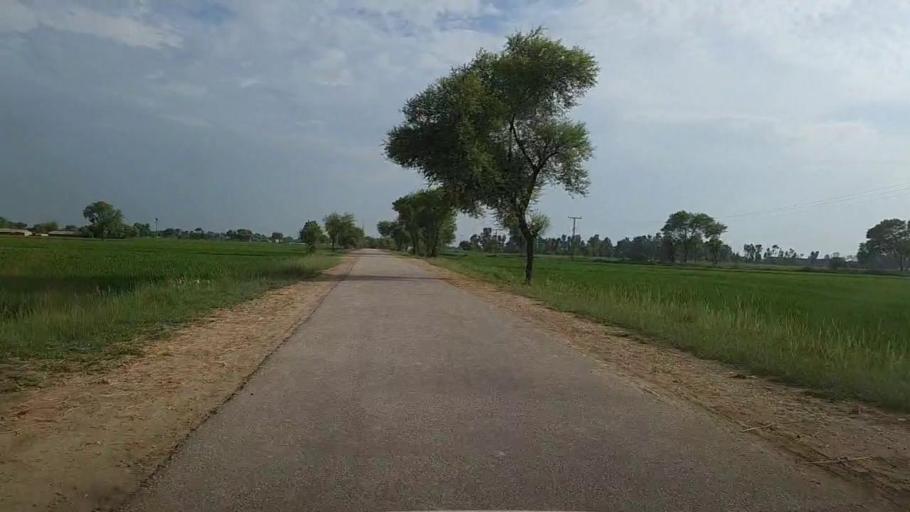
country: PK
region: Sindh
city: Thul
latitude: 28.2590
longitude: 68.8582
